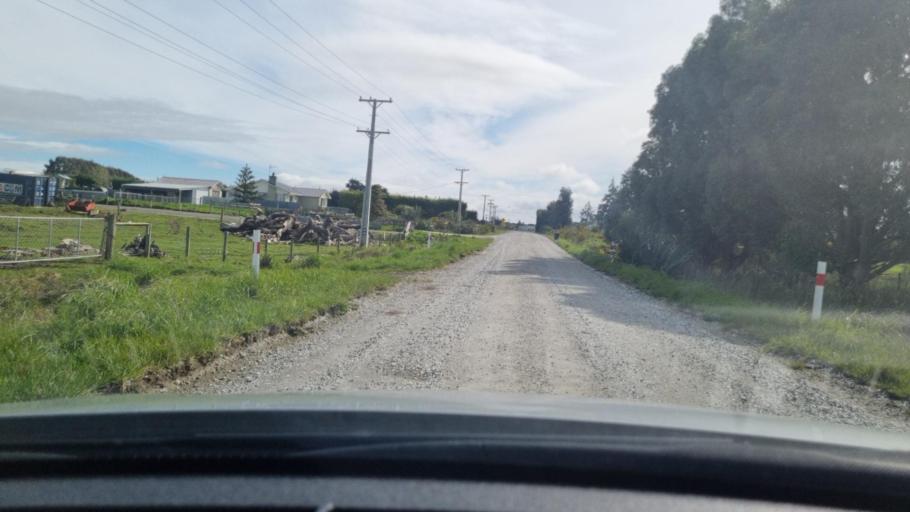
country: NZ
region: Southland
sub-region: Invercargill City
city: Invercargill
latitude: -46.4507
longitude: 168.3842
